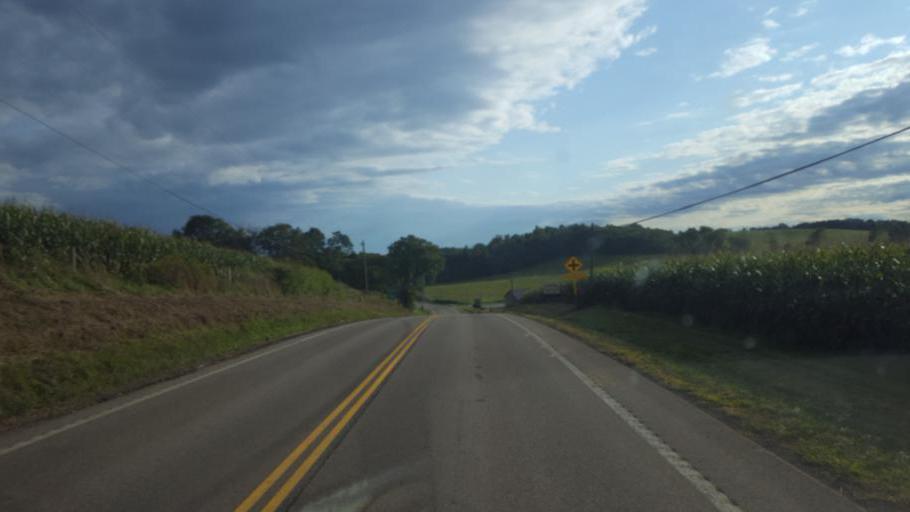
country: US
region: Ohio
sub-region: Knox County
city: Danville
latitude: 40.4243
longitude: -82.2671
